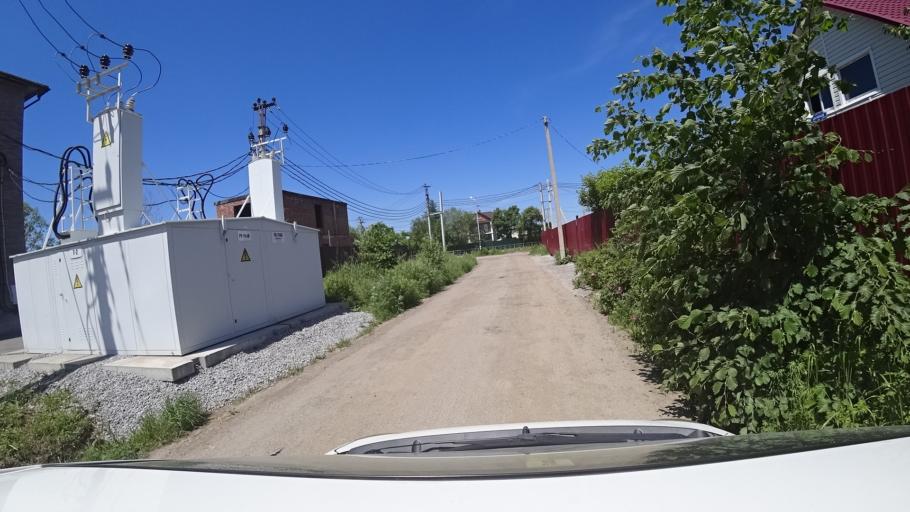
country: RU
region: Khabarovsk Krai
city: Topolevo
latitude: 48.5099
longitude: 135.1776
